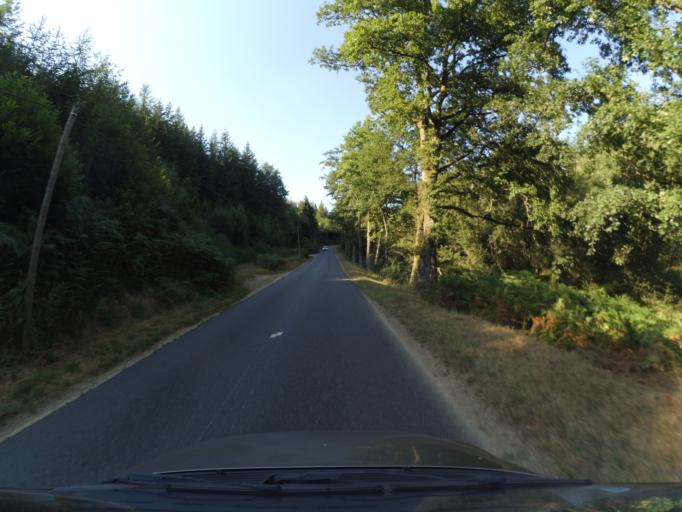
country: FR
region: Limousin
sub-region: Departement de la Haute-Vienne
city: Peyrat-le-Chateau
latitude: 45.7640
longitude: 1.8227
